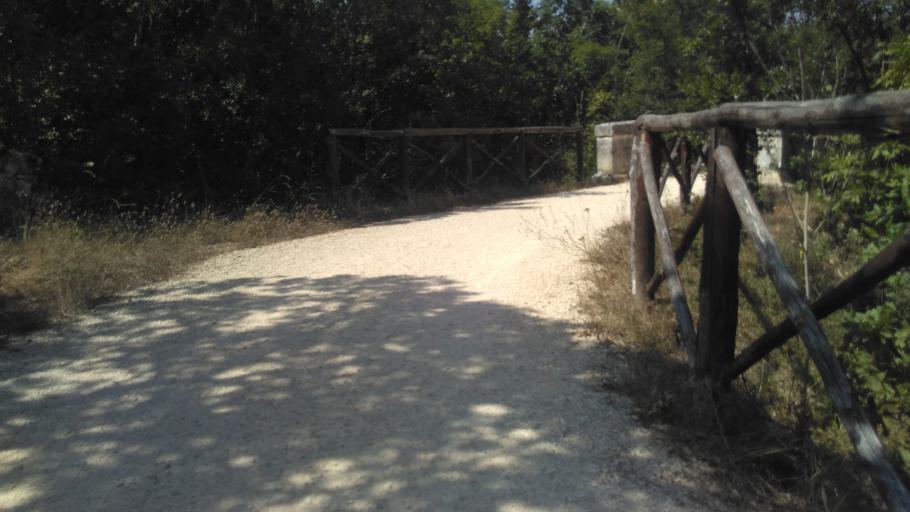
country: IT
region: Apulia
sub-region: Provincia di Brindisi
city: Cisternino
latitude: 40.6800
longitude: 17.4313
